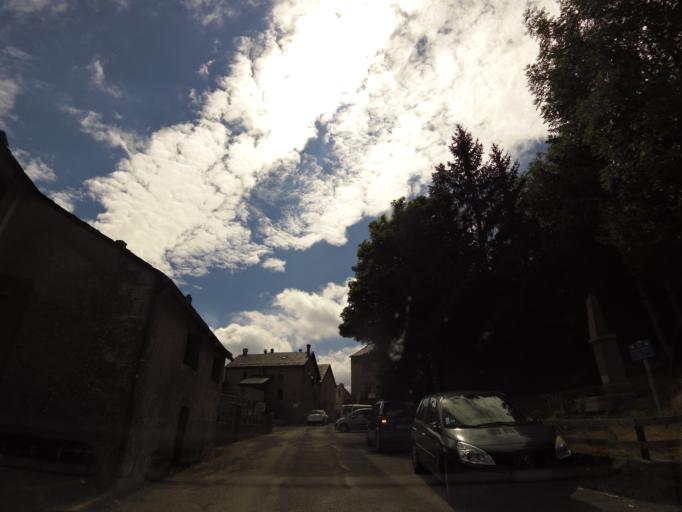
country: FR
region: Languedoc-Roussillon
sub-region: Departement de la Lozere
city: Meyrueis
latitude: 44.1156
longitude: 3.4768
